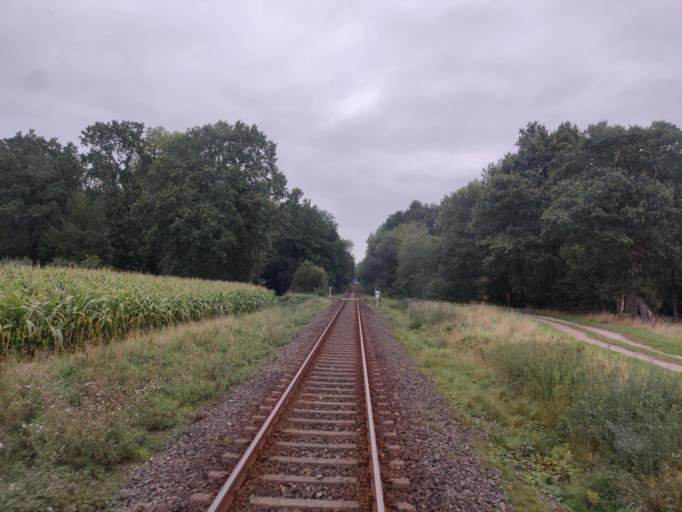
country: DE
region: Lower Saxony
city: Deinste
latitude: 53.5471
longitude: 9.4580
